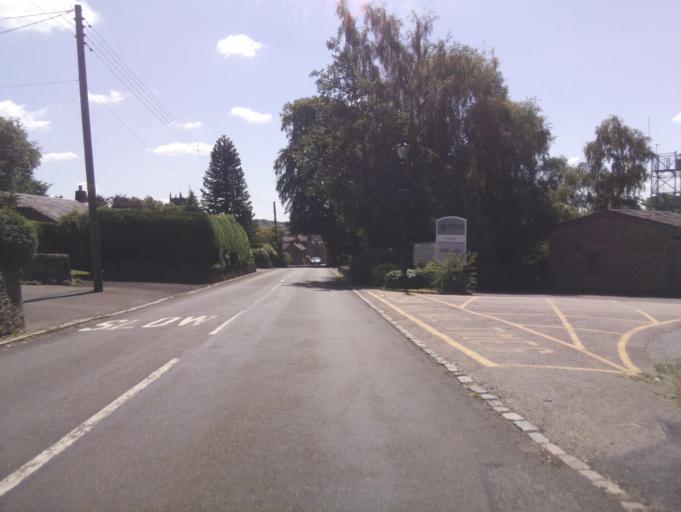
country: GB
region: England
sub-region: Derbyshire
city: Buxton
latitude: 53.1829
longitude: -1.8706
